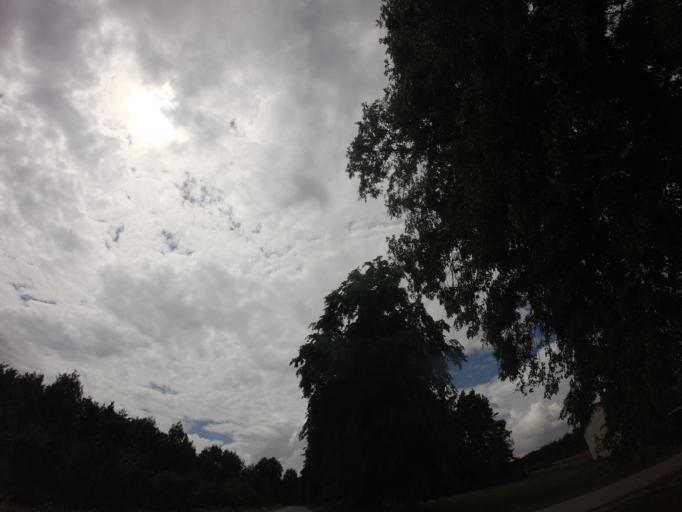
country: PL
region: Lublin Voivodeship
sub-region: Powiat pulawski
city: Kazimierz Dolny
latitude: 51.2941
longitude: 21.9476
